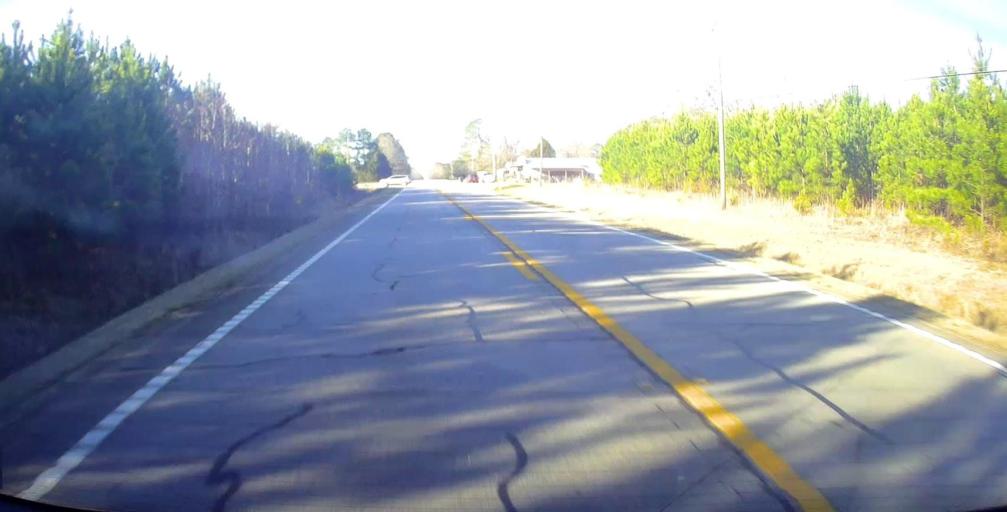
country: US
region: Georgia
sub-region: Meriwether County
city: Manchester
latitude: 32.8842
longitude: -84.5983
